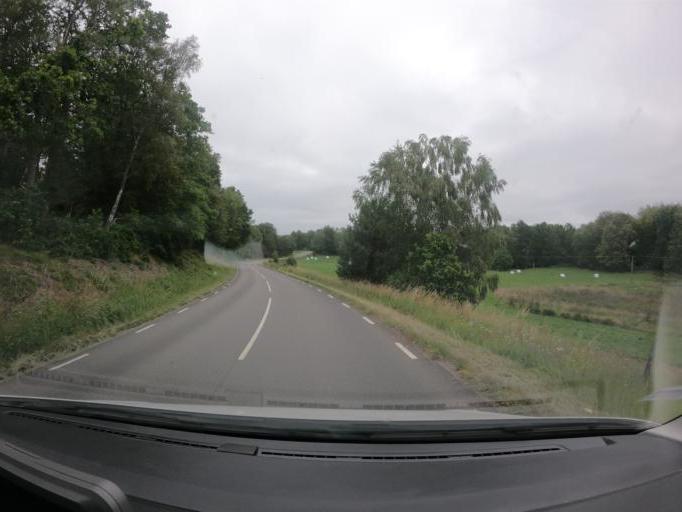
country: SE
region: Skane
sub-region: Perstorps Kommun
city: Perstorp
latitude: 56.0614
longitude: 13.3749
